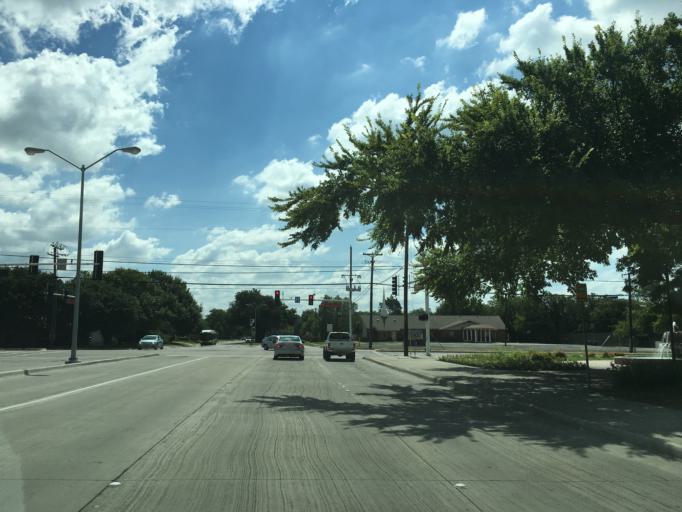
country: US
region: Texas
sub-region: Dallas County
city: Farmers Branch
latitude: 32.9243
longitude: -96.8739
